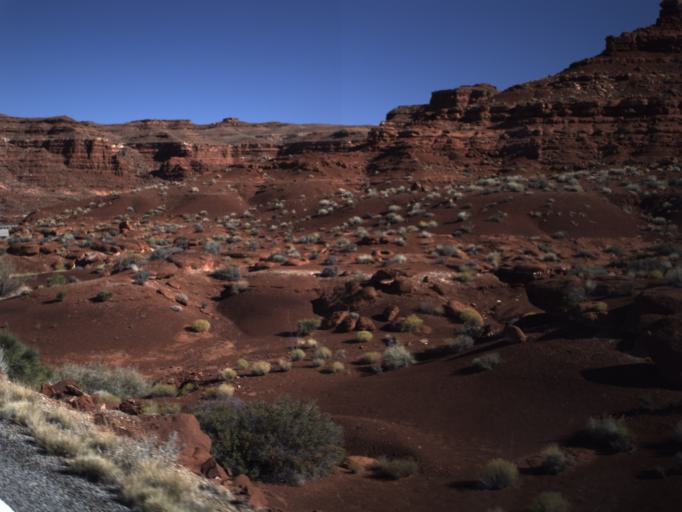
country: US
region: Utah
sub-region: San Juan County
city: Blanding
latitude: 37.8578
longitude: -110.3546
